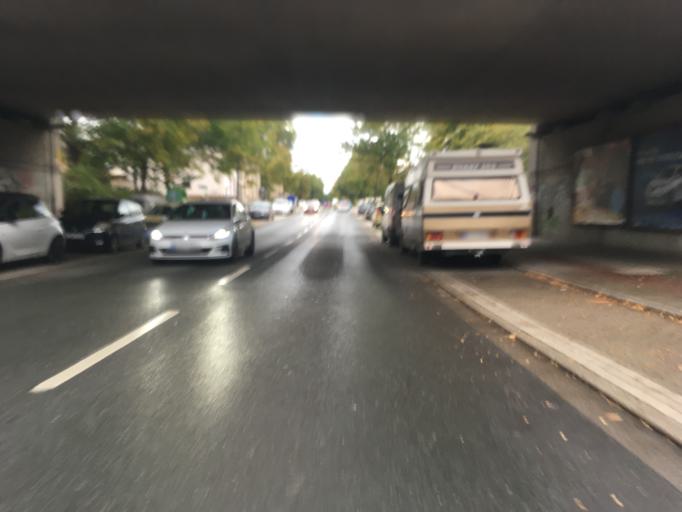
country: DE
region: North Rhine-Westphalia
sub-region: Regierungsbezirk Munster
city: Bottrop
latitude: 51.4883
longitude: 6.9332
